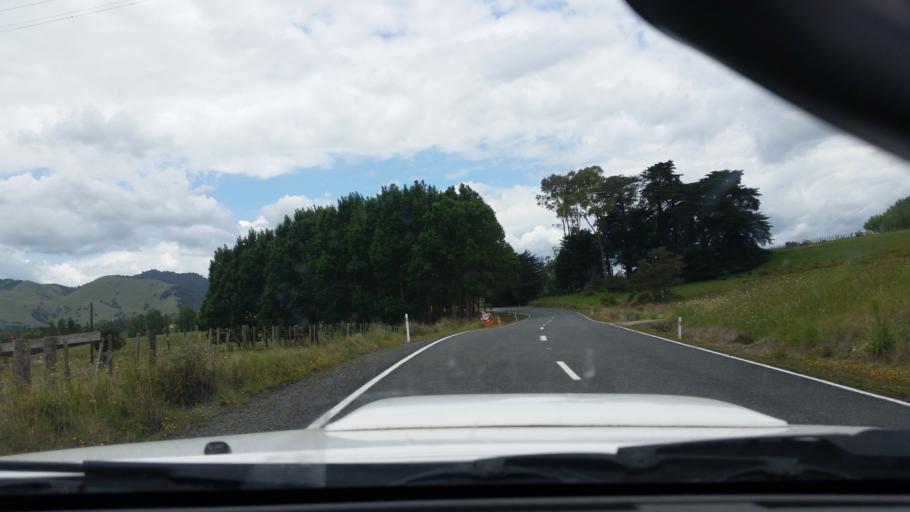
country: NZ
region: Northland
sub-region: Kaipara District
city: Dargaville
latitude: -35.7497
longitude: 173.8866
